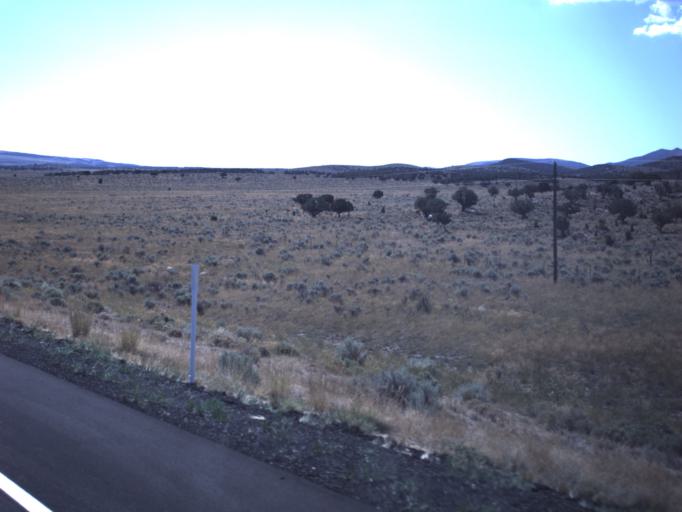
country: US
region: Utah
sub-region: Utah County
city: Eagle Mountain
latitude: 40.0667
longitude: -112.3242
